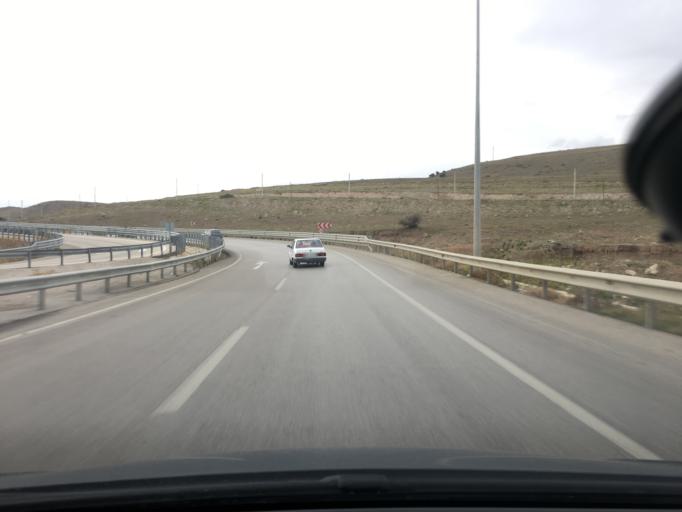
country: TR
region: Afyonkarahisar
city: Afyonkarahisar
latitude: 38.7965
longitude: 30.3919
